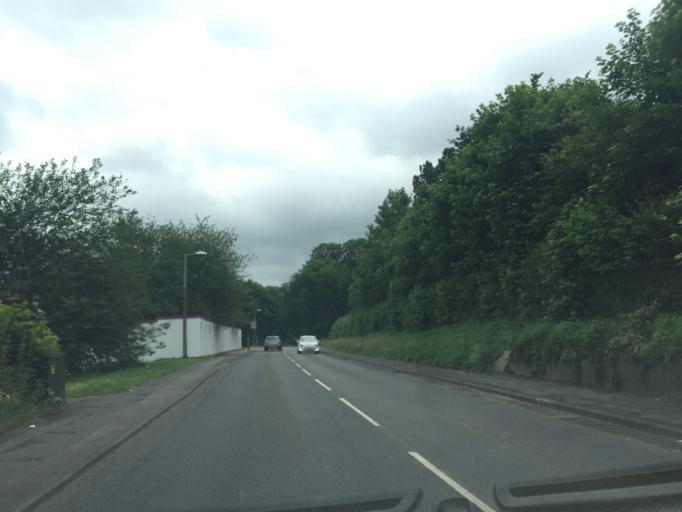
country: GB
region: England
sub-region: Essex
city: Harlow
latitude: 51.7502
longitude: 0.0833
